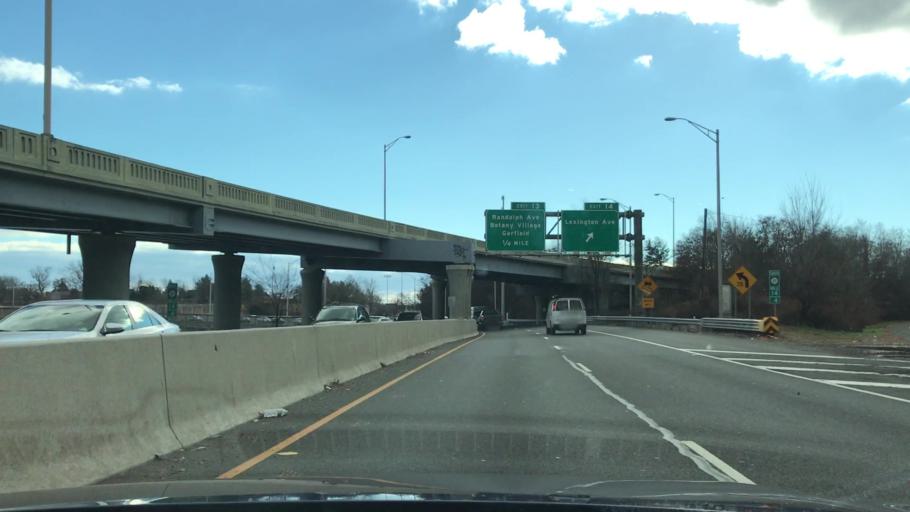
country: US
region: New Jersey
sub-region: Bergen County
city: Garfield
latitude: 40.8869
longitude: -74.1319
